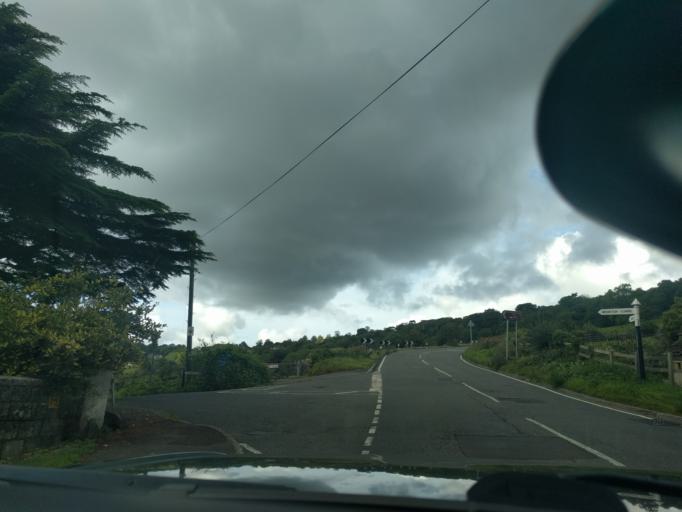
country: GB
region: England
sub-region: Bath and North East Somerset
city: Freshford
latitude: 51.3595
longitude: -2.3175
